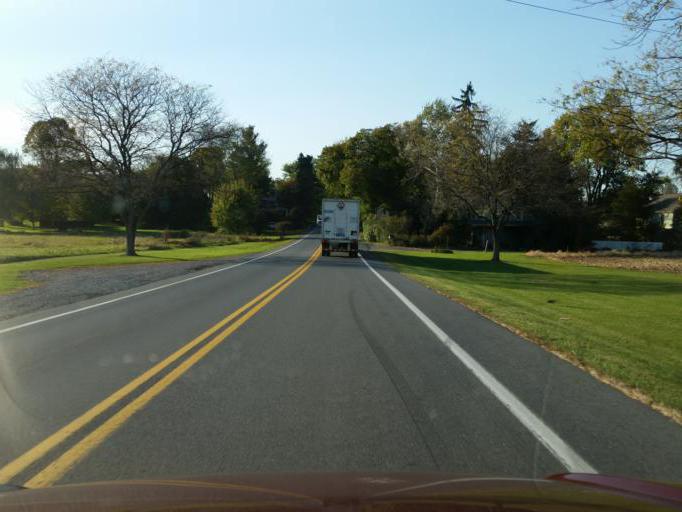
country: US
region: Pennsylvania
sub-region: Dauphin County
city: Hershey
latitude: 40.2552
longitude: -76.6308
